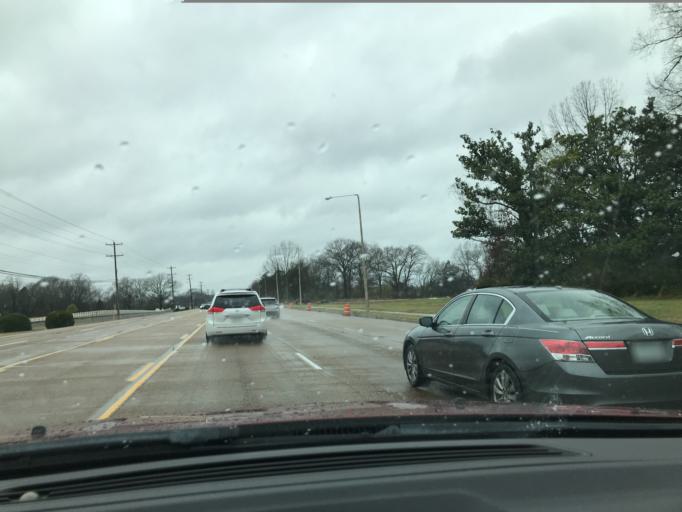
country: US
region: Tennessee
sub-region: Shelby County
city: Collierville
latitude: 35.0466
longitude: -89.7060
